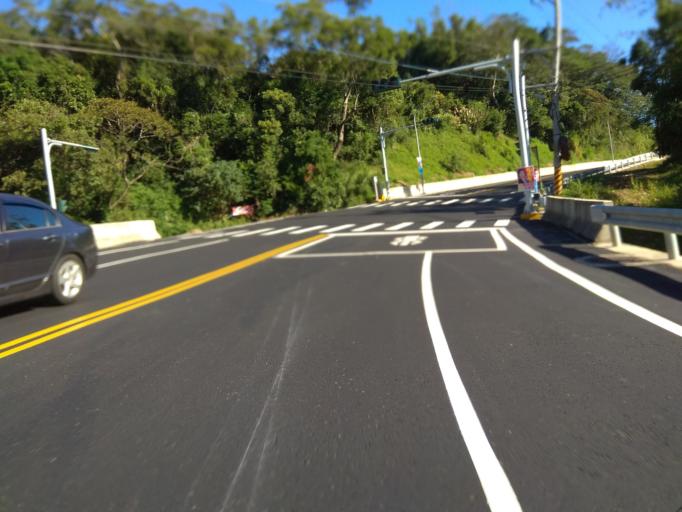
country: TW
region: Taiwan
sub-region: Hsinchu
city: Zhubei
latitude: 24.8501
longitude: 121.1177
